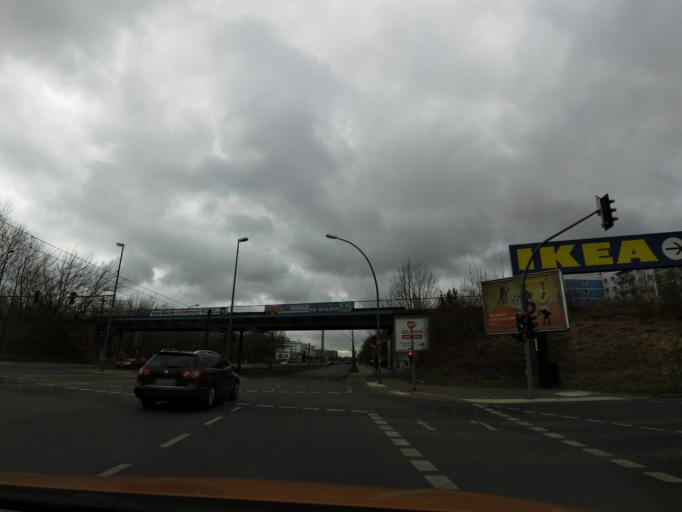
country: DE
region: Berlin
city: Alt-Hohenschoenhausen
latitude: 52.5330
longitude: 13.5187
